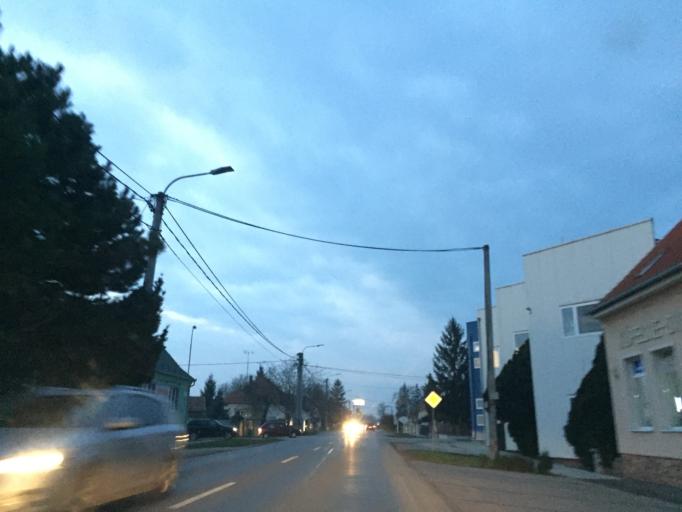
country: SK
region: Nitriansky
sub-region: Okres Nove Zamky
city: Nove Zamky
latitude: 47.9963
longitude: 18.1583
